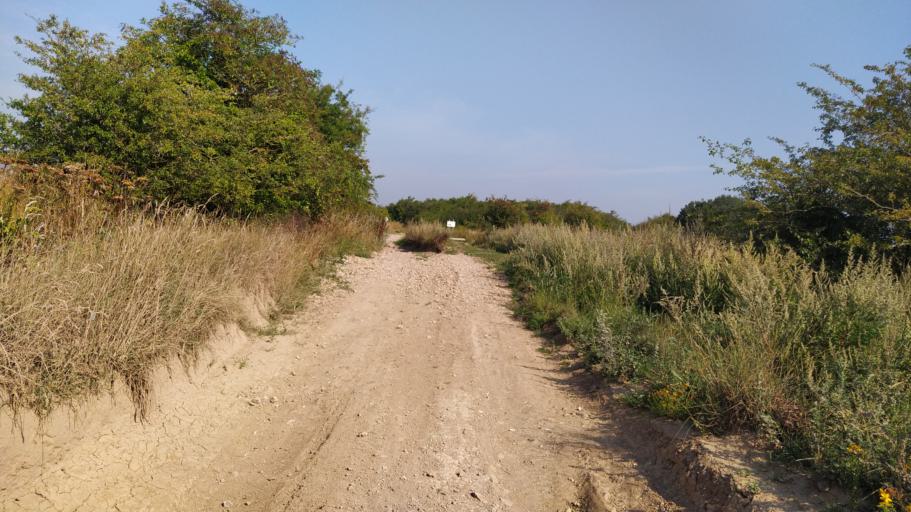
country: GB
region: England
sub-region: Wiltshire
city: Winterbourne Stoke
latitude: 51.1681
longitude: -1.9520
